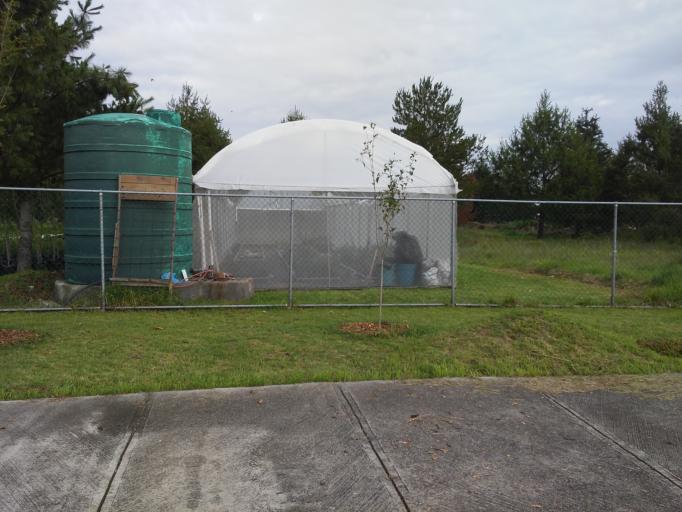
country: MX
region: Mexico
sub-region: Metepec
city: San Salvador Tizatlalli
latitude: 19.2482
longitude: -99.5871
